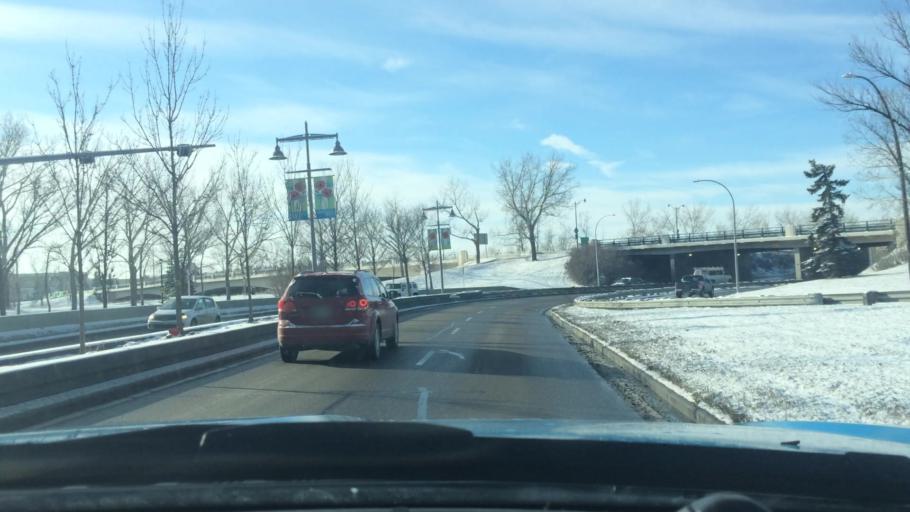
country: CA
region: Alberta
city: Calgary
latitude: 51.0498
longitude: -114.0931
